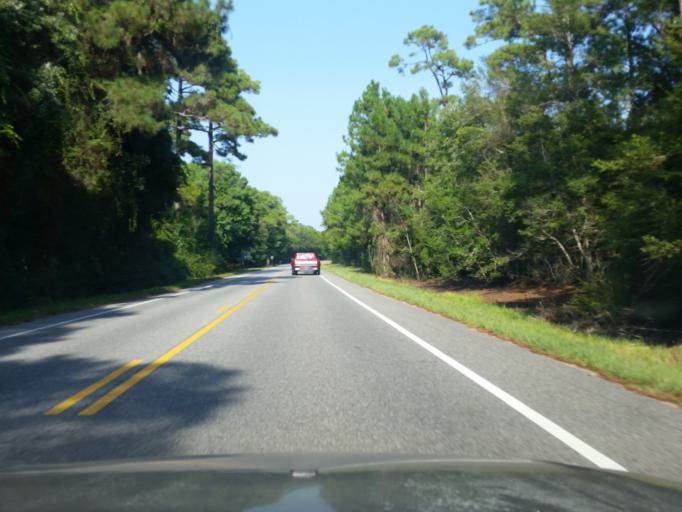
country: US
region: Alabama
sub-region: Baldwin County
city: Gulf Shores
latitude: 30.2520
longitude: -87.8088
